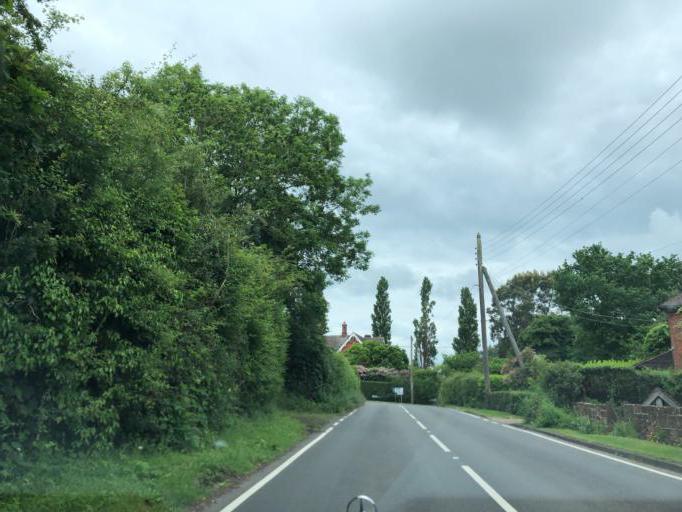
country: GB
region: England
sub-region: Solihull
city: Berkswell
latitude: 52.3946
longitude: -1.6142
